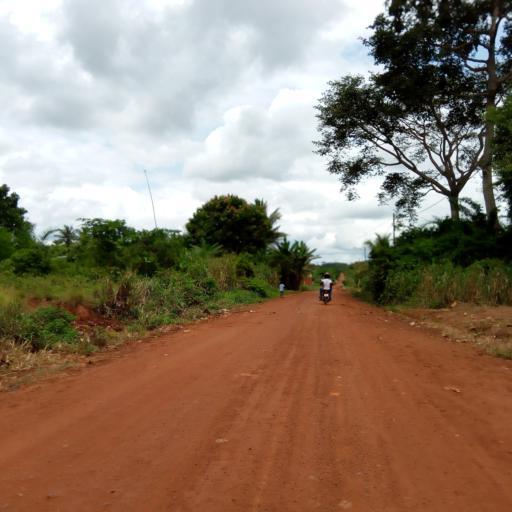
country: TG
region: Maritime
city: Tsevie
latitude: 6.3404
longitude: 1.1049
